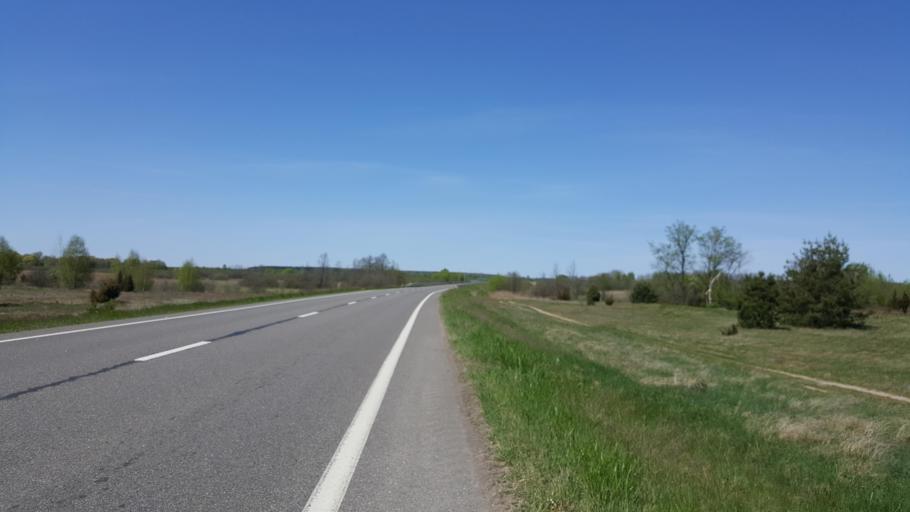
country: BY
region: Brest
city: Kamyanyets
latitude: 52.4241
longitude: 23.8395
